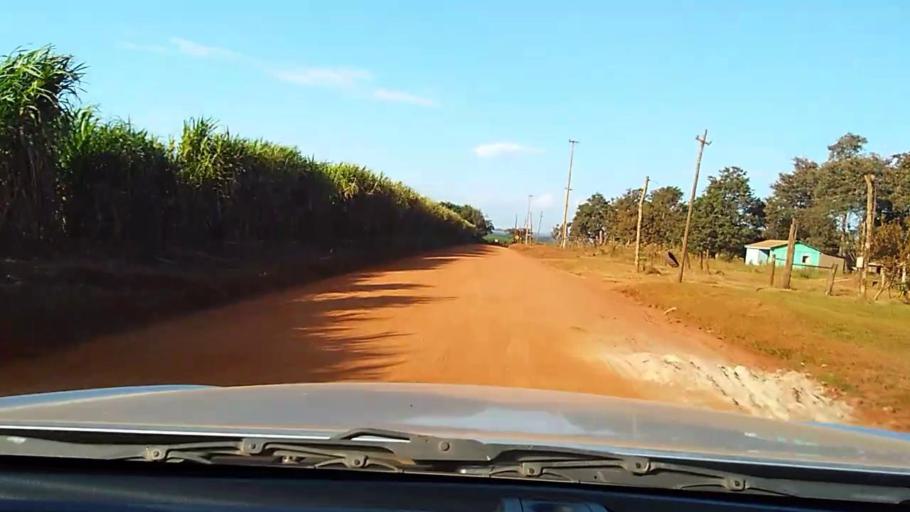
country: PY
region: Alto Parana
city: Doctor Juan Leon Mallorquin
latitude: -25.6940
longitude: -55.3785
